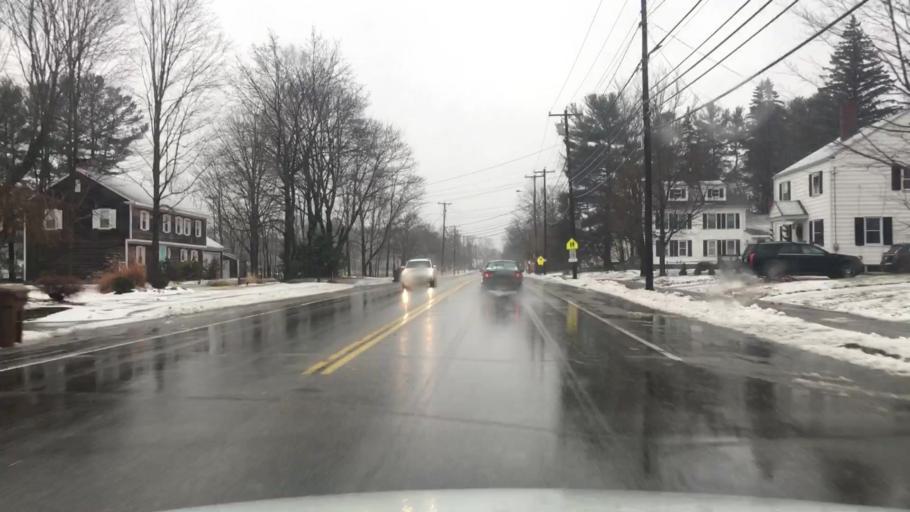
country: US
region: Maine
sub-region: York County
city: Saco
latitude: 43.5106
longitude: -70.4495
